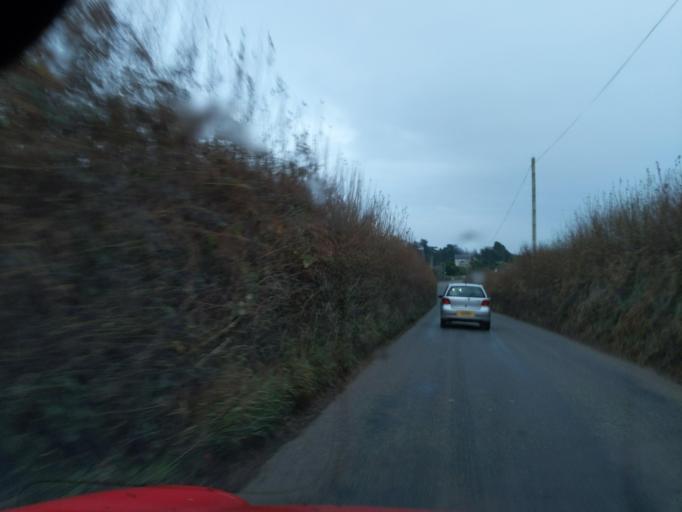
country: GB
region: England
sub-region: Devon
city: Wembury
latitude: 50.3428
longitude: -4.0752
